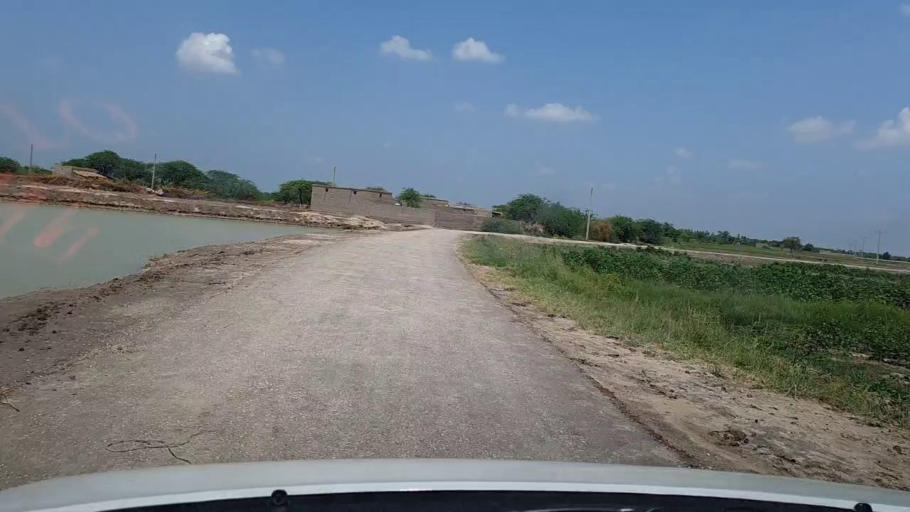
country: PK
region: Sindh
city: Kandiaro
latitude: 26.9870
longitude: 68.2253
